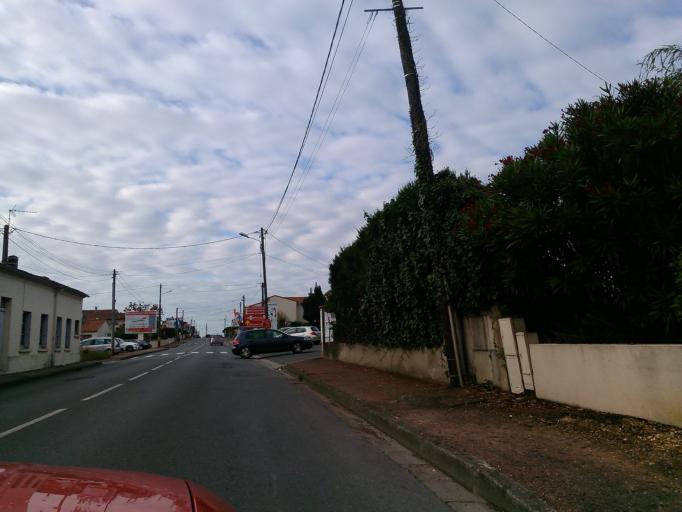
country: FR
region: Poitou-Charentes
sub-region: Departement de la Charente-Maritime
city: Royan
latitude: 45.6441
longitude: -1.0249
